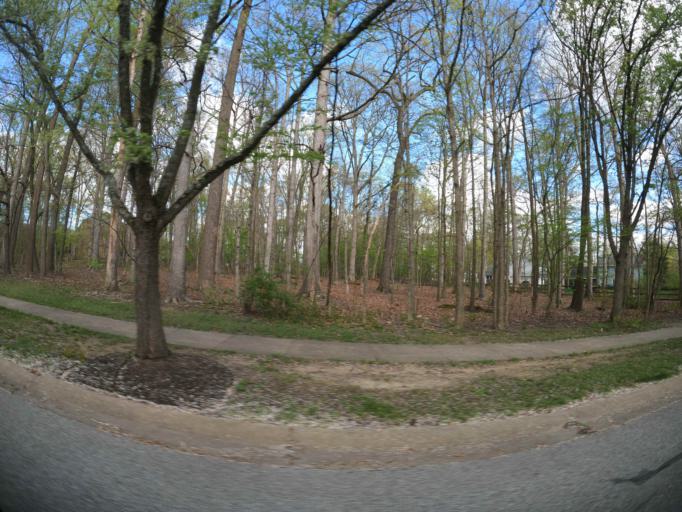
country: US
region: Maryland
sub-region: Howard County
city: Riverside
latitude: 39.2094
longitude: -76.8849
